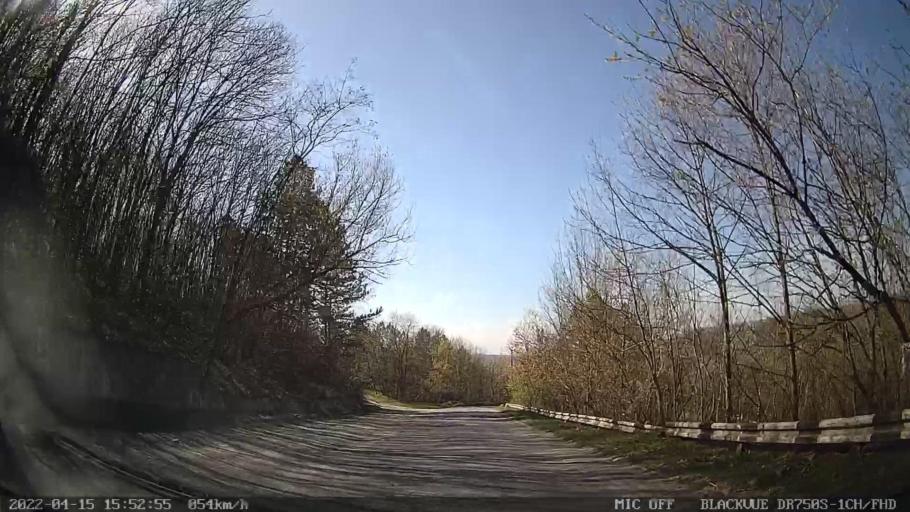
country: MD
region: Raionul Ocnita
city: Otaci
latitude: 48.3966
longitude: 27.8892
